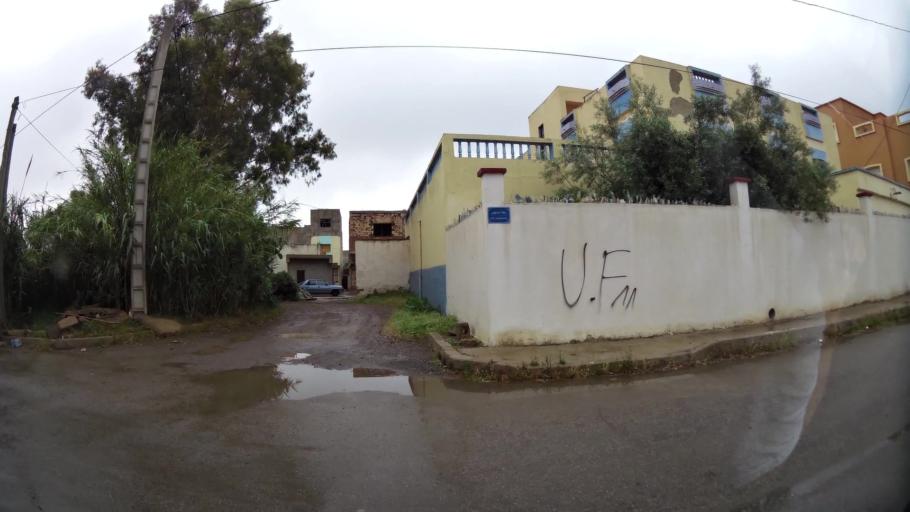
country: MA
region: Oriental
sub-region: Nador
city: Nador
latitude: 35.1582
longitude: -2.9709
